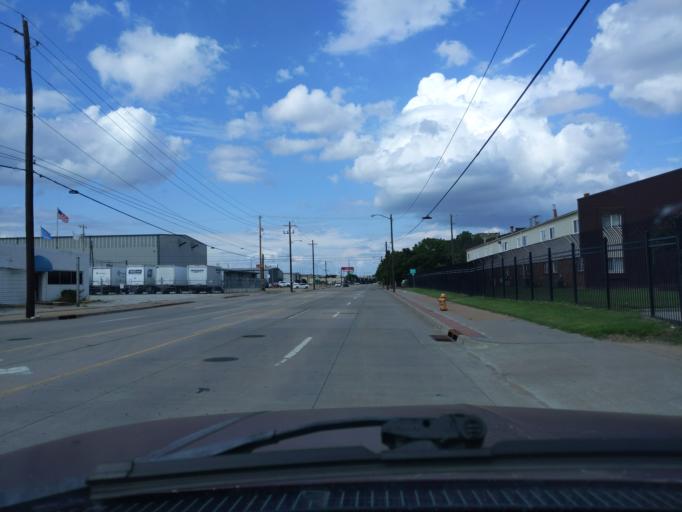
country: US
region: Oklahoma
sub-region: Tulsa County
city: Tulsa
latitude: 36.1324
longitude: -96.0069
